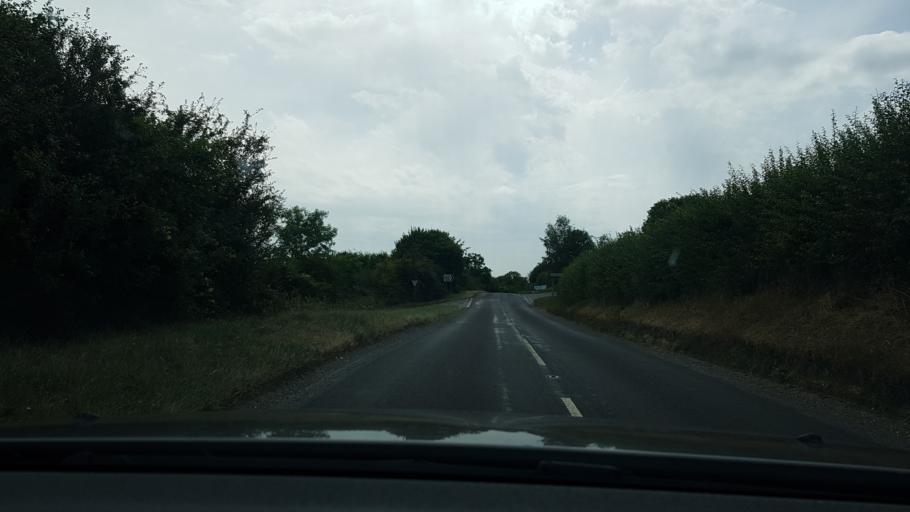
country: GB
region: England
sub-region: Wiltshire
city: Shalbourne
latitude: 51.3632
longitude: -1.5618
